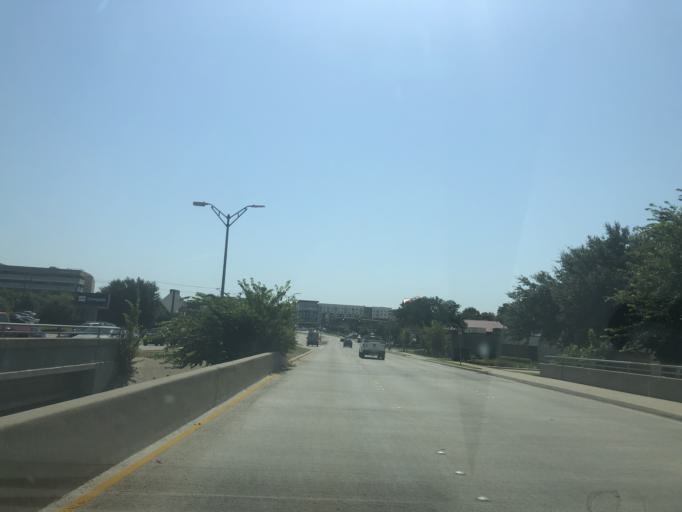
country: US
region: Texas
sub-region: Tarrant County
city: Fort Worth
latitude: 32.7337
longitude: -97.3489
